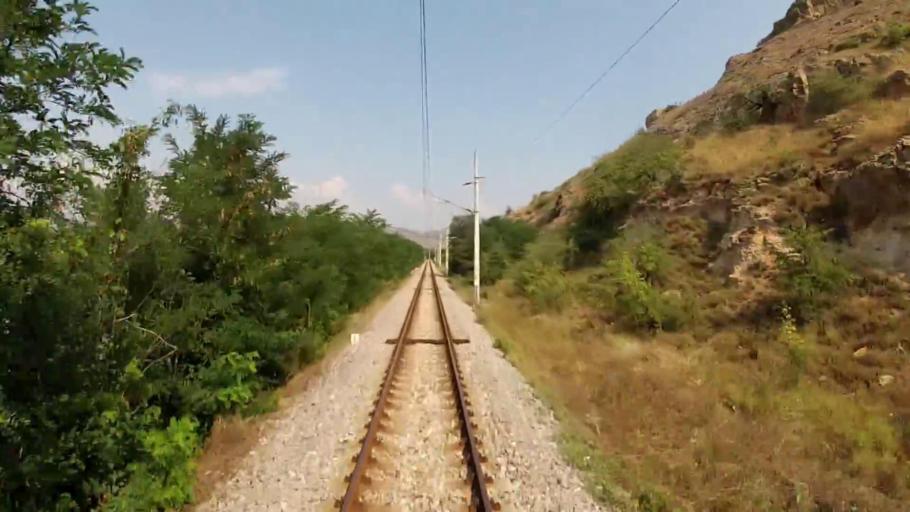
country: BG
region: Blagoevgrad
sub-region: Obshtina Sandanski
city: Sandanski
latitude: 41.4910
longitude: 23.2682
